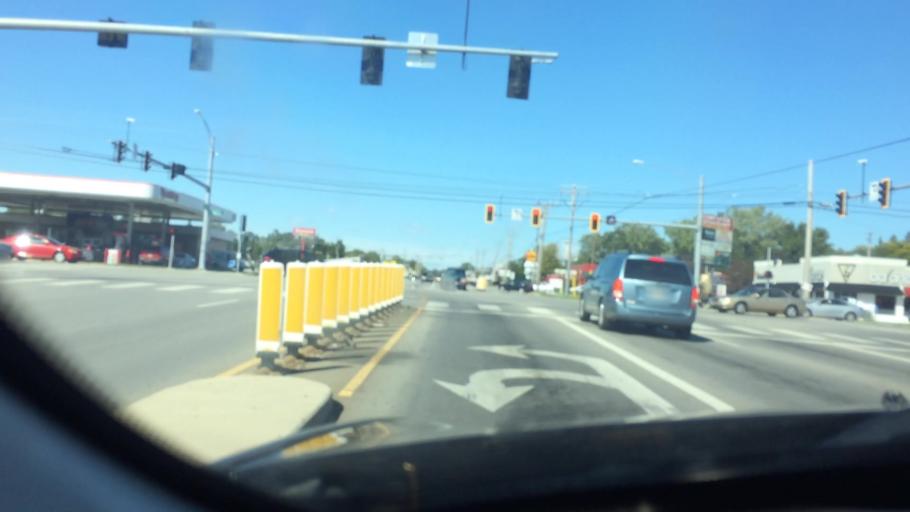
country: US
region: Ohio
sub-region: Lucas County
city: Ottawa Hills
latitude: 41.6758
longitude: -83.6827
